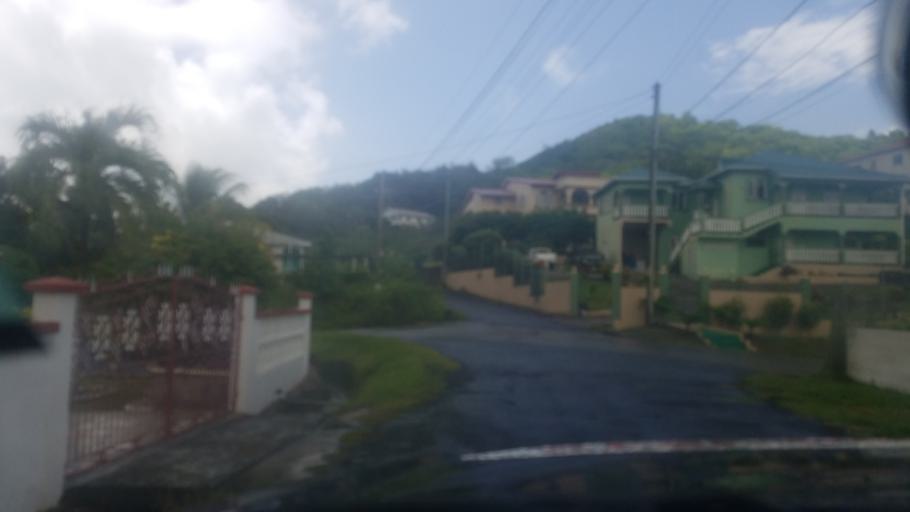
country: LC
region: Laborie Quarter
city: Laborie
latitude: 13.7462
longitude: -60.9677
